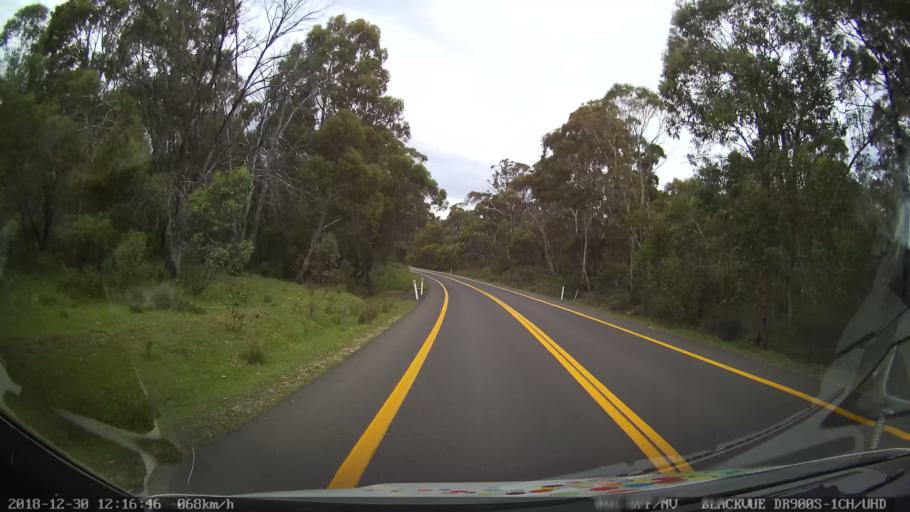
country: AU
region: New South Wales
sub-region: Snowy River
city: Jindabyne
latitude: -36.3481
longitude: 148.5635
